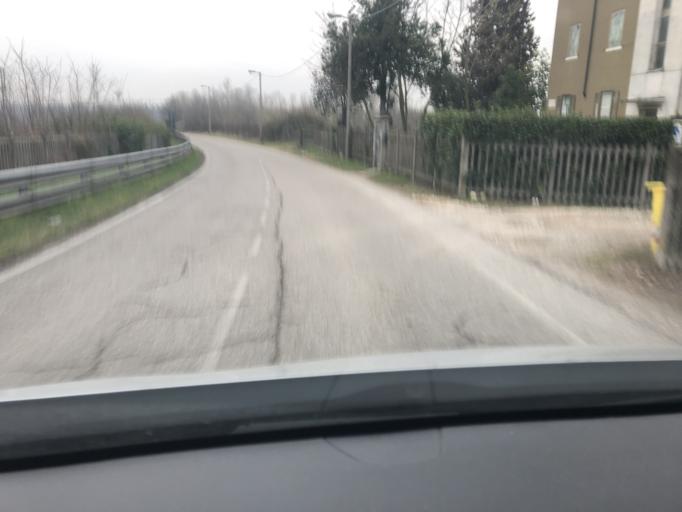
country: IT
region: Veneto
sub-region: Provincia di Verona
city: Verona
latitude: 45.4304
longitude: 10.9526
